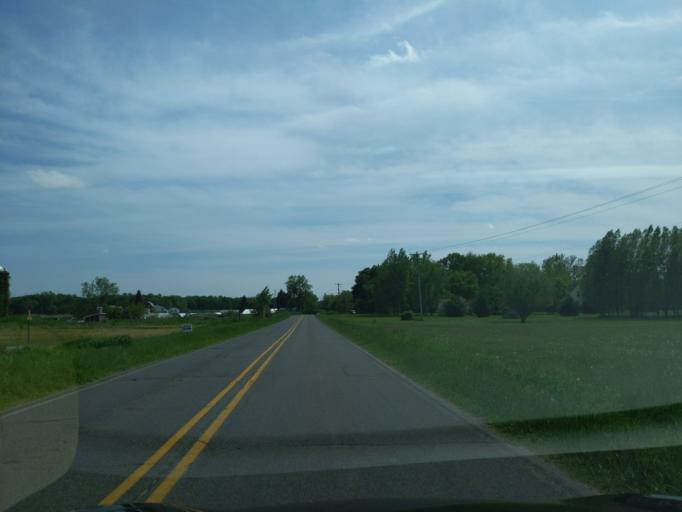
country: US
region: Michigan
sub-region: Ingham County
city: Leslie
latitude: 42.4149
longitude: -84.3130
